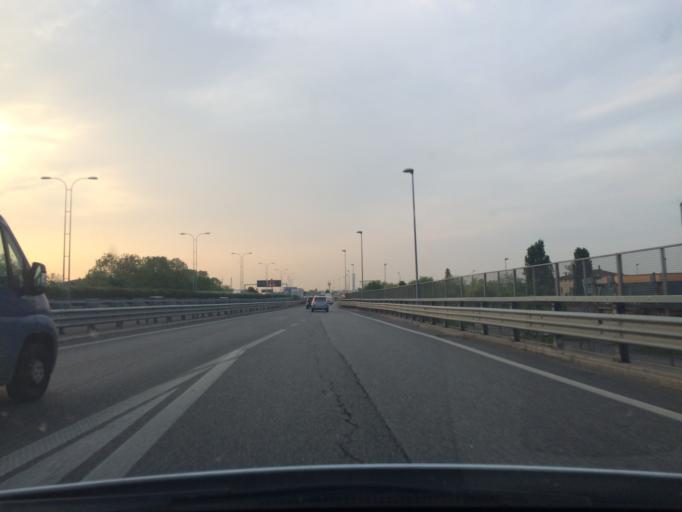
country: IT
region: Lombardy
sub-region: Provincia di Brescia
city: Roncadelle
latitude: 45.5243
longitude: 10.1783
